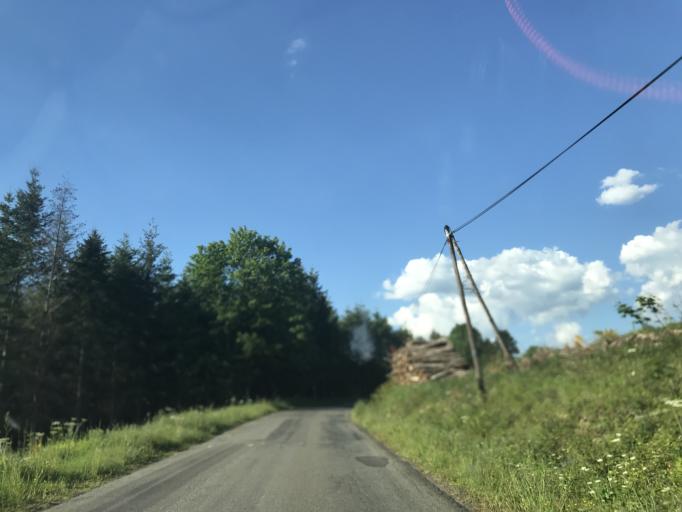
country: FR
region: Auvergne
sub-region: Departement du Puy-de-Dome
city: Job
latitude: 45.6152
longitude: 3.6775
